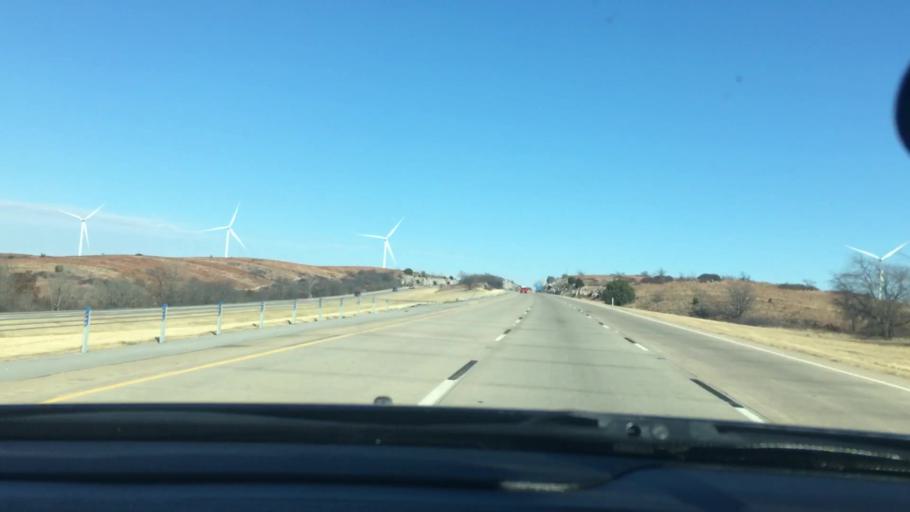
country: US
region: Oklahoma
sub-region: Murray County
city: Davis
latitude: 34.3649
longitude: -97.1467
